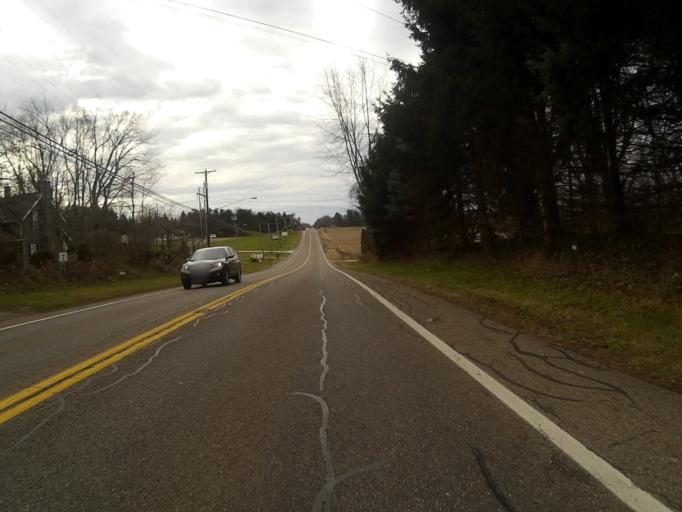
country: US
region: Ohio
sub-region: Portage County
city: Brimfield
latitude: 41.0888
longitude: -81.3467
